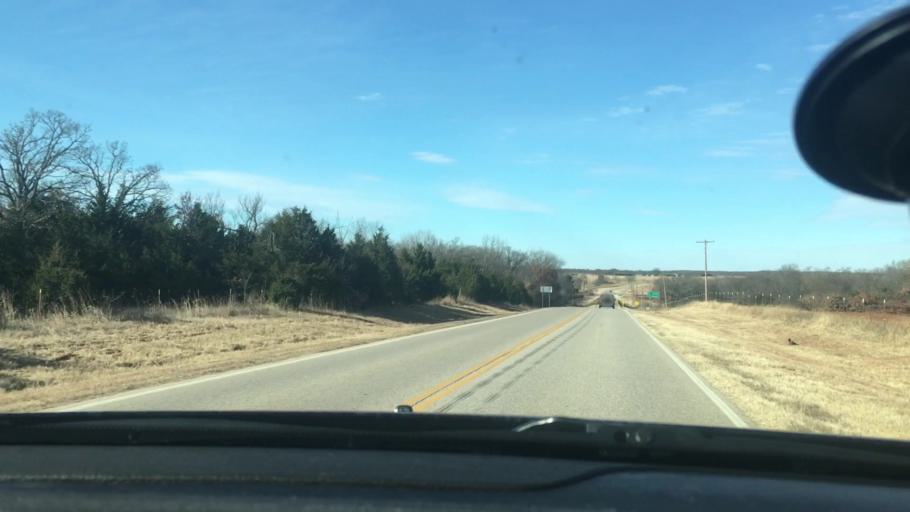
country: US
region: Oklahoma
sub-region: Garvin County
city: Stratford
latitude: 34.9859
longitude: -97.0300
